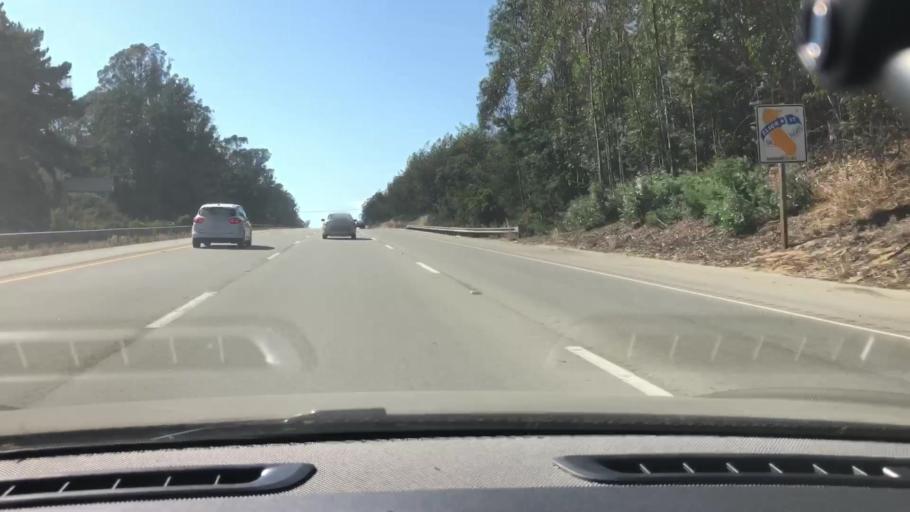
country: US
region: California
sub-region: Santa Cruz County
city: Aptos Hills-Larkin Valley
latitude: 36.9333
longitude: -121.8161
